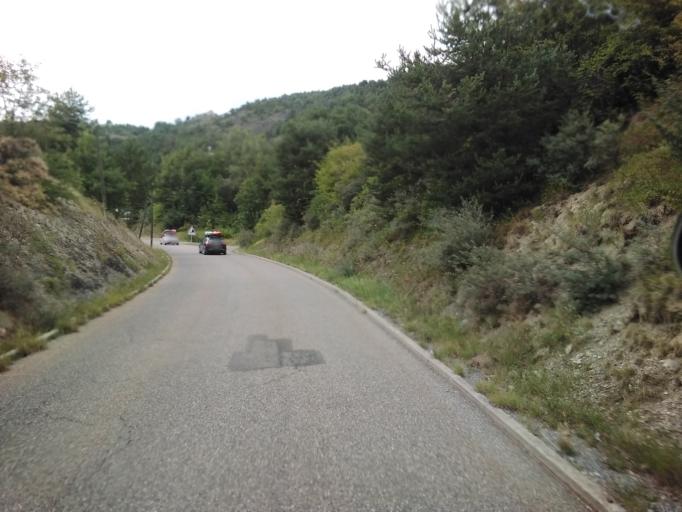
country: FR
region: Provence-Alpes-Cote d'Azur
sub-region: Departement des Alpes-de-Haute-Provence
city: Seyne-les-Alpes
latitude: 44.4550
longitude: 6.3870
